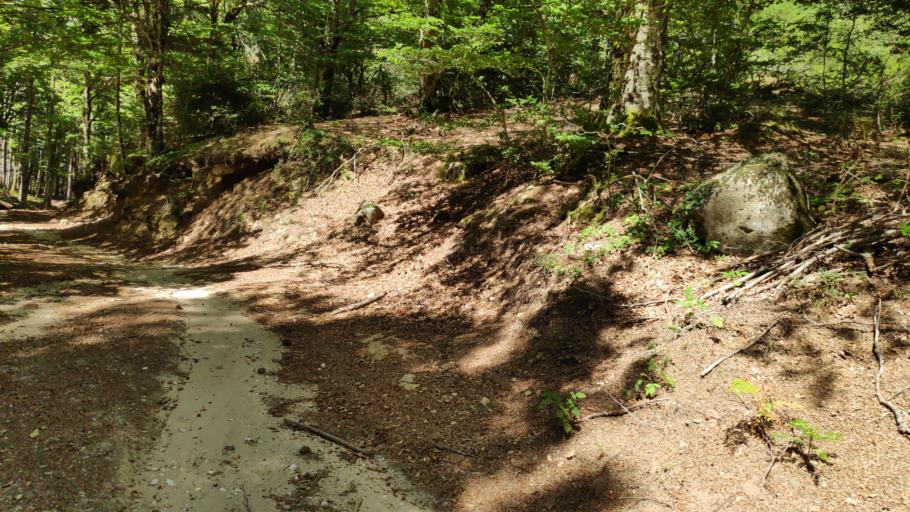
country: IT
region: Calabria
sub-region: Provincia di Vibo-Valentia
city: Serra San Bruno
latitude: 38.5393
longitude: 16.3873
